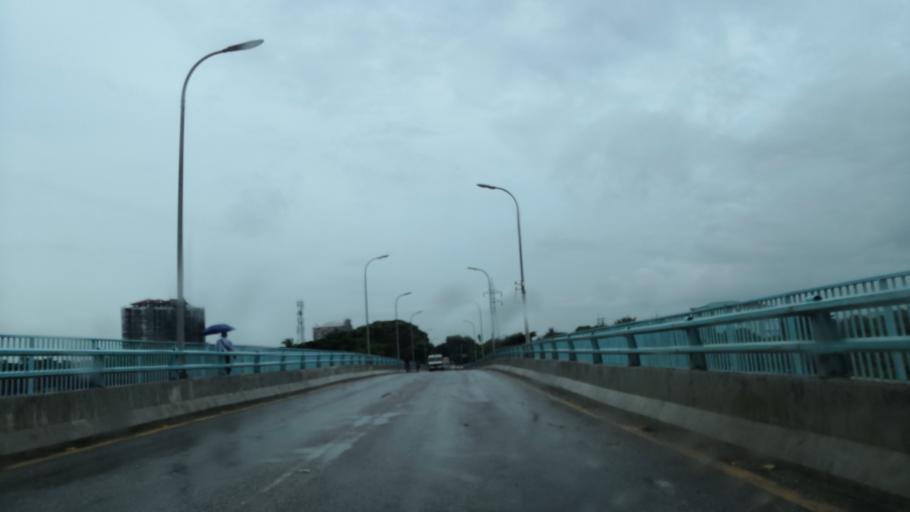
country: MM
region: Yangon
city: Yangon
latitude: 16.8049
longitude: 96.1871
